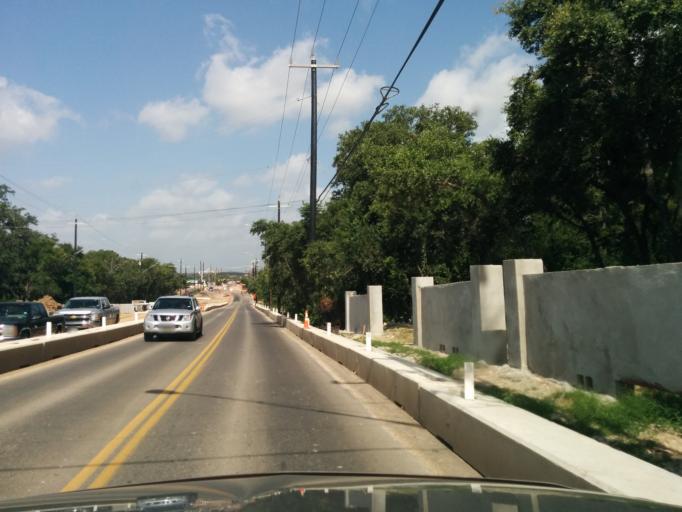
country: US
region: Texas
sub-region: Bexar County
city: Helotes
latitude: 29.5723
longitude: -98.6266
